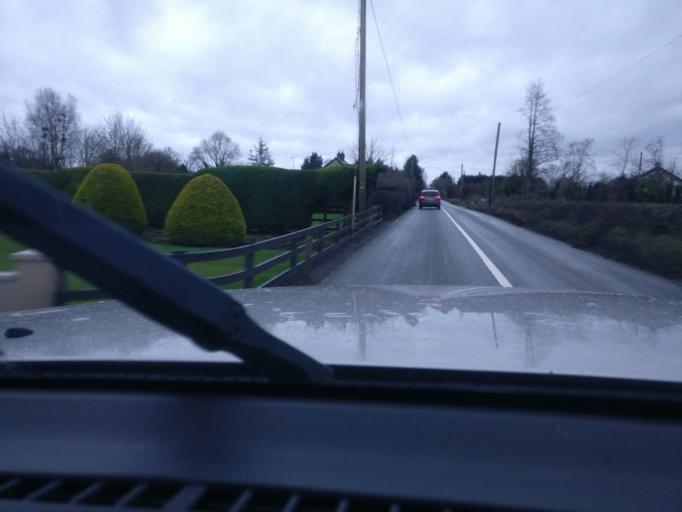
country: IE
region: Leinster
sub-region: An Mhi
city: Longwood
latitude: 53.4690
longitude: -6.9101
